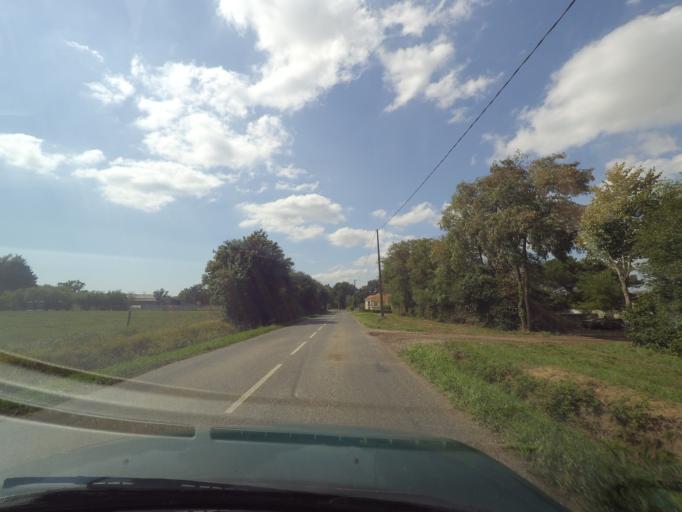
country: FR
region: Pays de la Loire
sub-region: Departement de la Loire-Atlantique
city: Sainte-Pazanne
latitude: 47.0987
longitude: -1.8308
